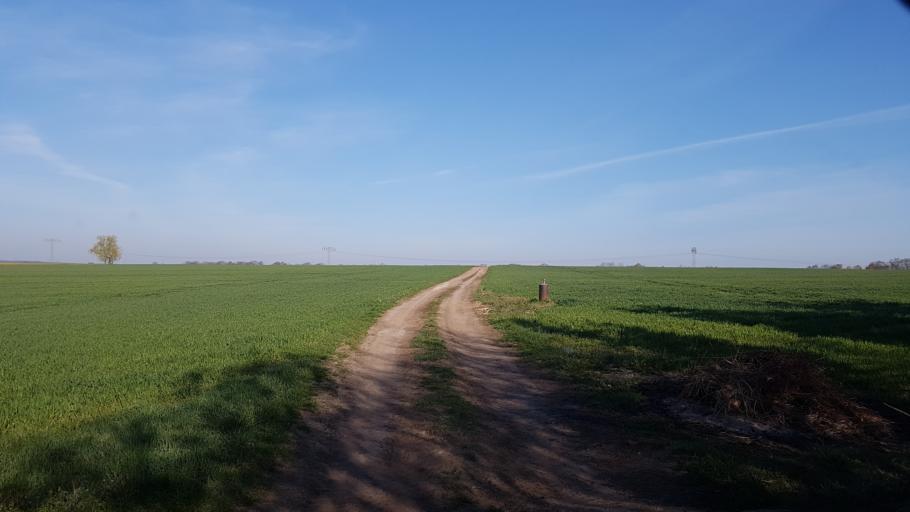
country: DE
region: Brandenburg
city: Doberlug-Kirchhain
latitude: 51.6185
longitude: 13.5855
